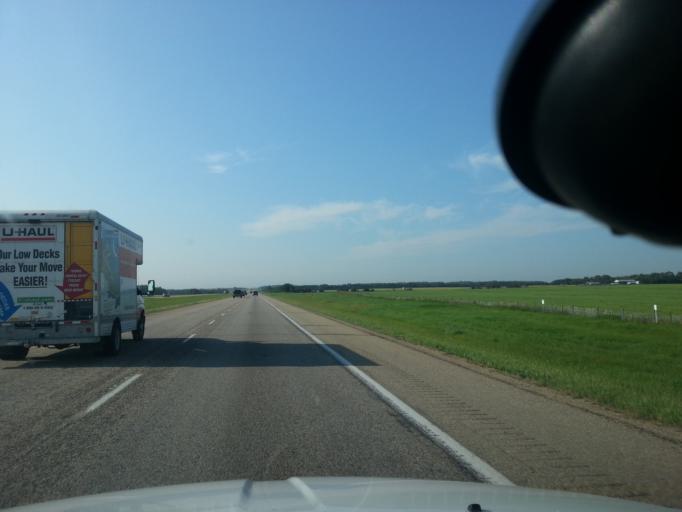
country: CA
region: Alberta
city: Ponoka
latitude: 52.8706
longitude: -113.6442
